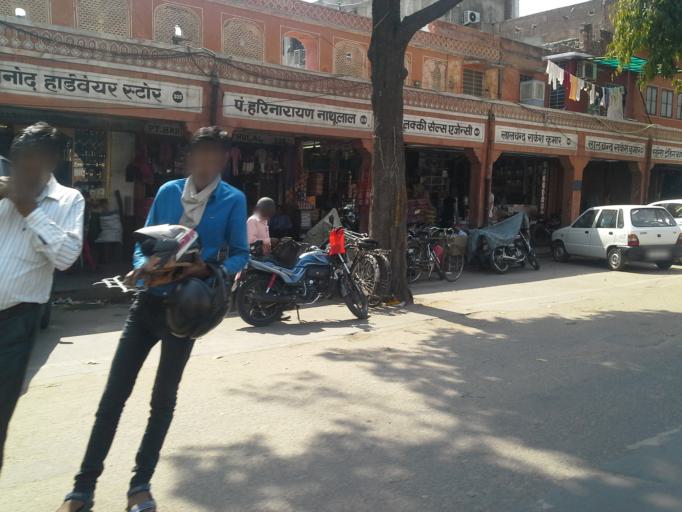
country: IN
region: Rajasthan
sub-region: Jaipur
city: Jaipur
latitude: 26.9241
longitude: 75.8211
